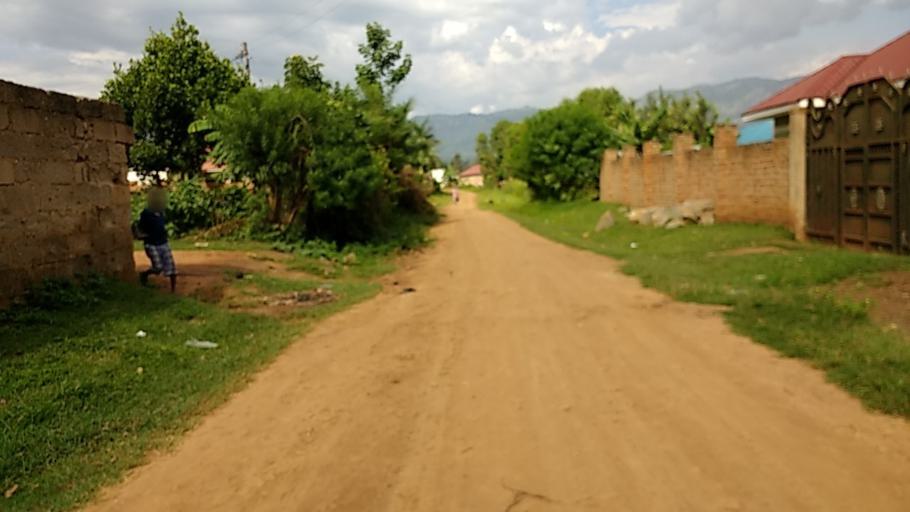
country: UG
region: Eastern Region
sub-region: Mbale District
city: Mbale
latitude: 1.0664
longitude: 34.1682
